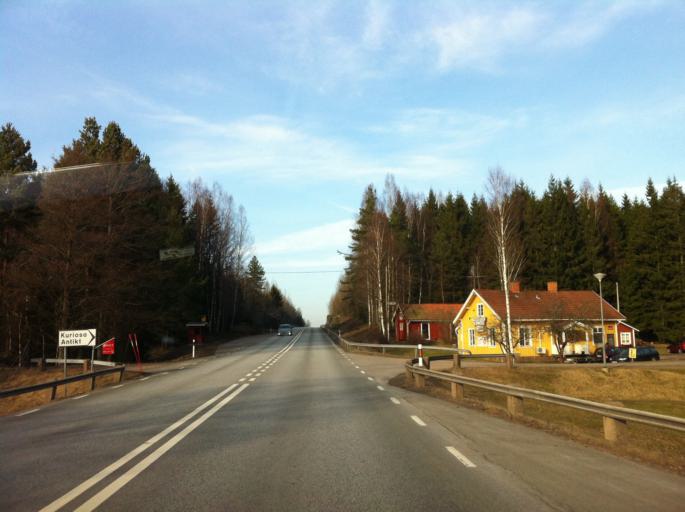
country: SE
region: Vaermland
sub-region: Storfors Kommun
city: Storfors
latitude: 59.4421
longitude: 14.2358
